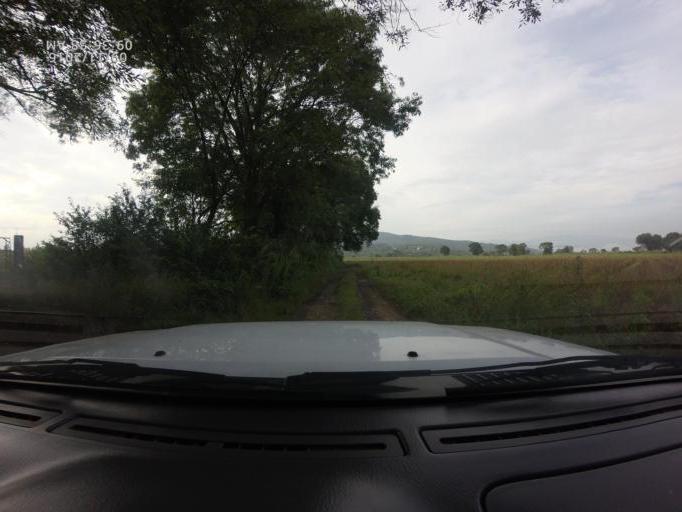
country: MX
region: Michoacan
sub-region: Morelia
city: La Mintzita (Piedra Dura)
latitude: 19.5704
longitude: -101.2905
